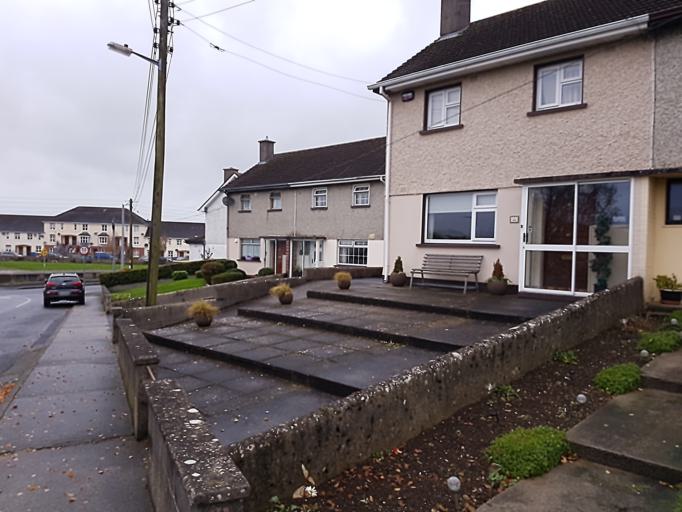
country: IE
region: Leinster
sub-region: Kilkenny
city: Kilkenny
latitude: 52.6566
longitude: -7.2375
